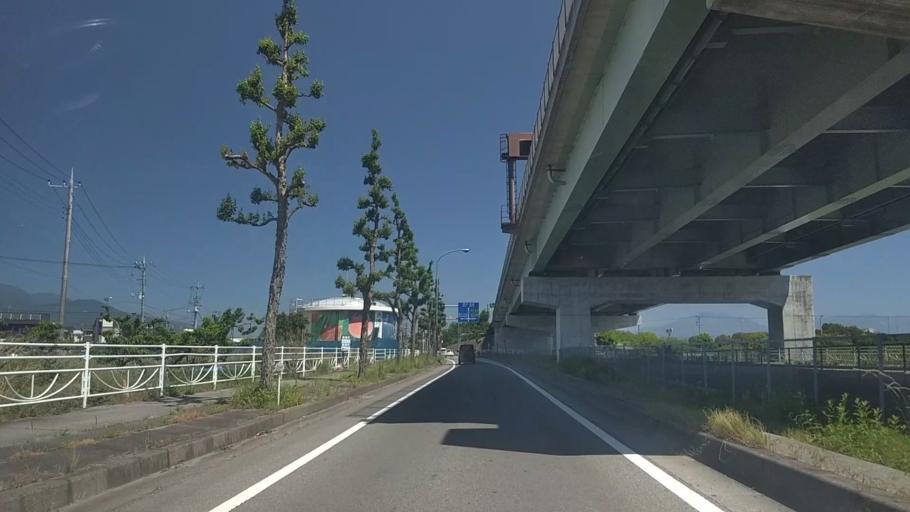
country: JP
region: Yamanashi
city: Ryuo
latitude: 35.6117
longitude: 138.4805
